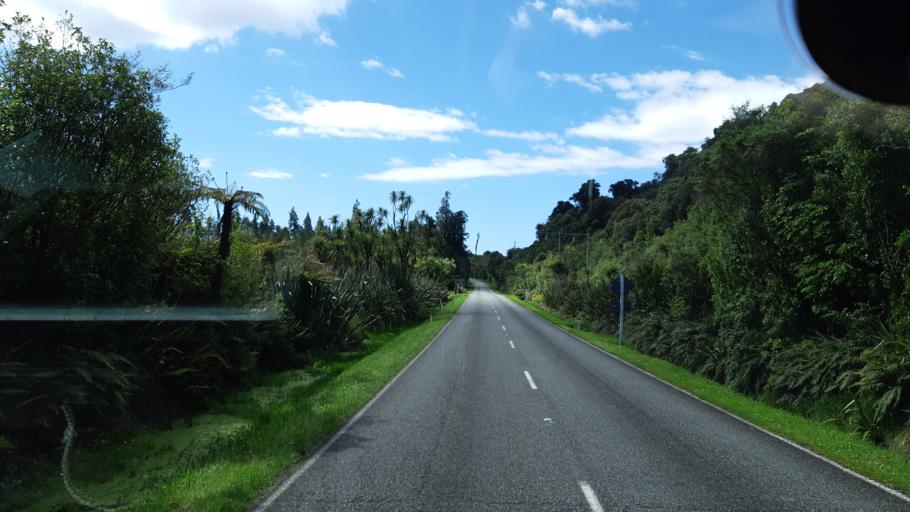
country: NZ
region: West Coast
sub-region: Westland District
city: Hokitika
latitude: -43.0768
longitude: 170.6262
